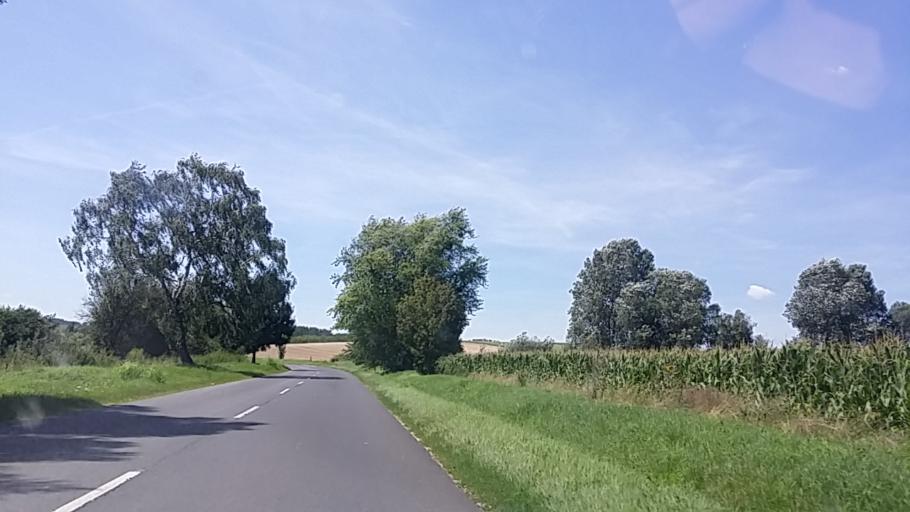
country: HU
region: Somogy
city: Tab
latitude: 46.7194
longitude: 17.9629
